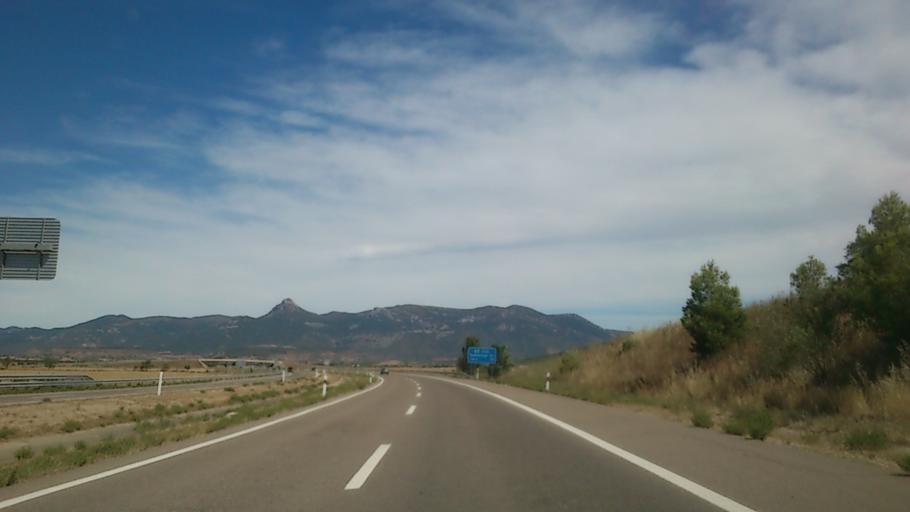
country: ES
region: Aragon
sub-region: Provincia de Huesca
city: Banastas
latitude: 42.1849
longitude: -0.4308
